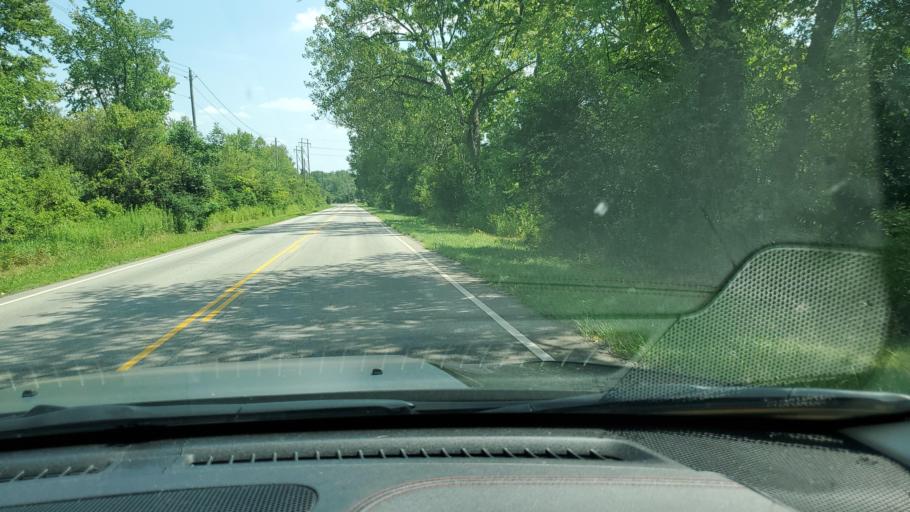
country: US
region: Ohio
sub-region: Trumbull County
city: Bolindale
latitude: 41.2083
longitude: -80.8021
